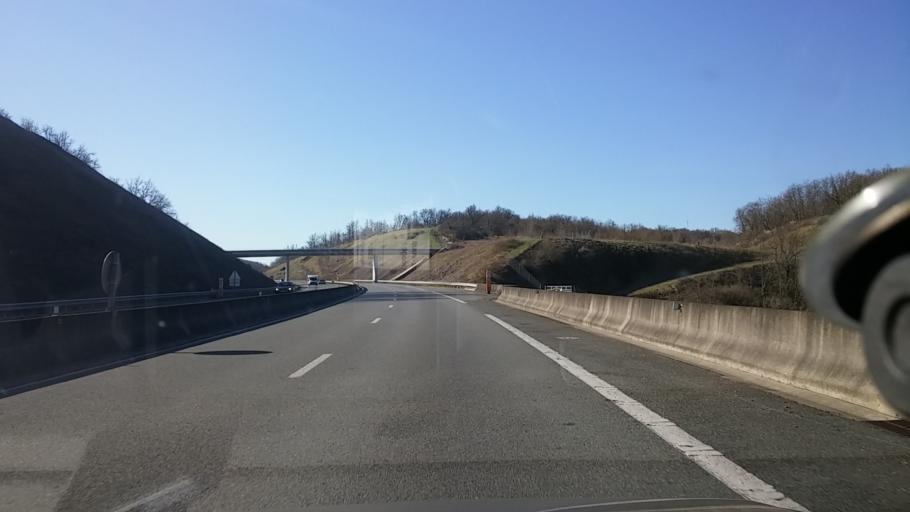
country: FR
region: Midi-Pyrenees
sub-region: Departement du Lot
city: Souillac
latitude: 44.8444
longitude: 1.4911
